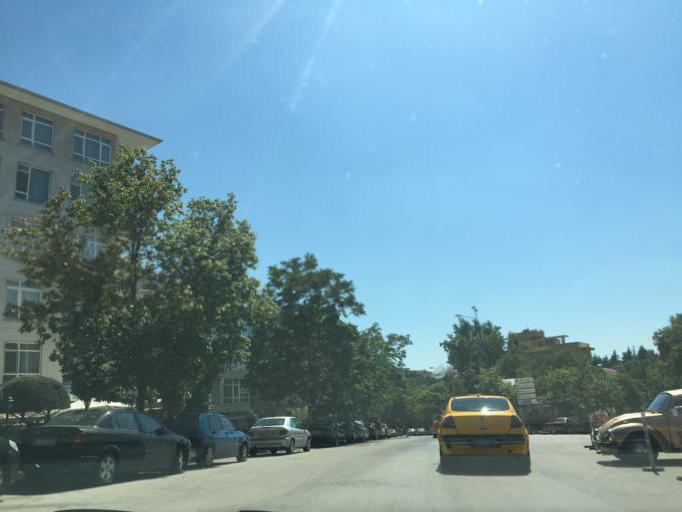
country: TR
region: Ankara
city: Ankara
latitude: 39.9079
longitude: 32.8548
